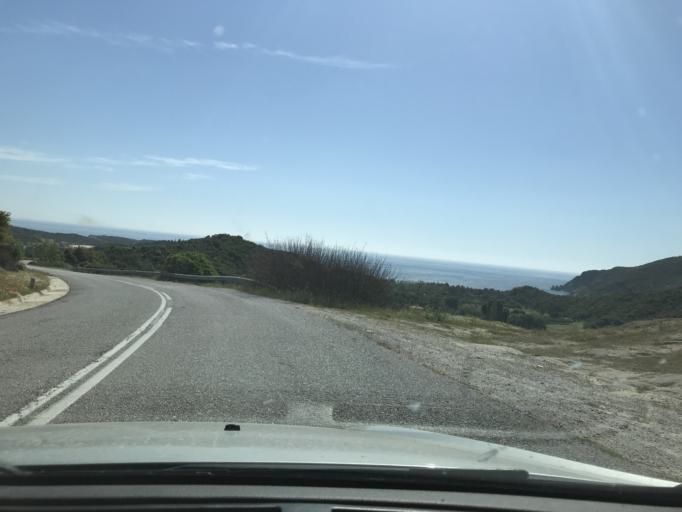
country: GR
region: Central Macedonia
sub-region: Nomos Chalkidikis
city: Sykia
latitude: 39.9894
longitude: 23.9770
